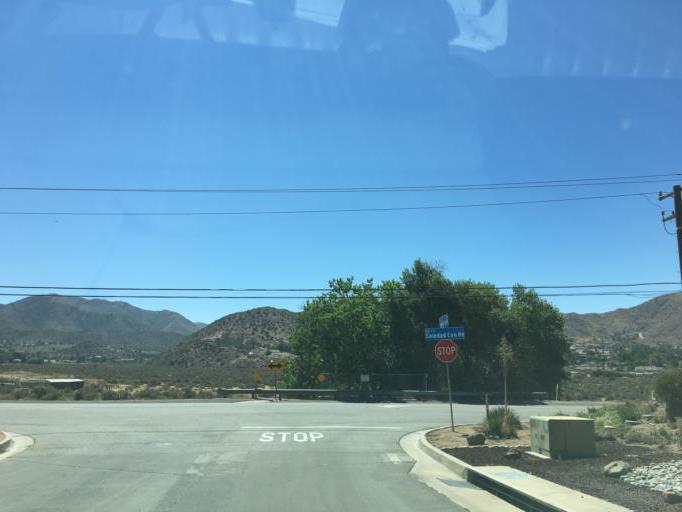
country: US
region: California
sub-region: Los Angeles County
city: Acton
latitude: 34.4743
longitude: -118.1731
